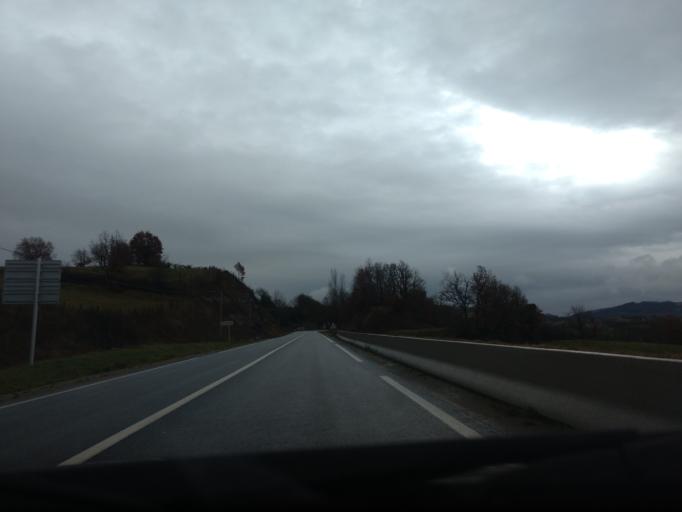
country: FR
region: Midi-Pyrenees
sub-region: Departement de l'Aveyron
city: Firmi
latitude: 44.5118
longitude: 2.3599
